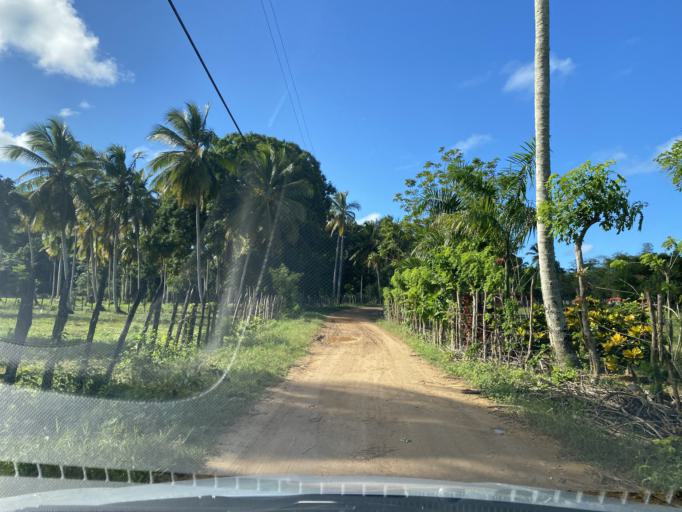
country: DO
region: Samana
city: Las Terrenas
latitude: 19.3084
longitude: -69.5580
